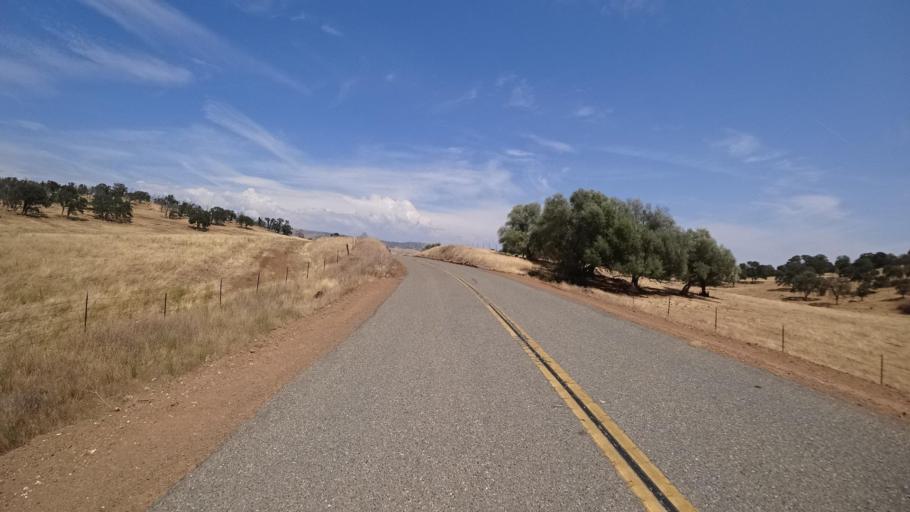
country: US
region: California
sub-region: Merced County
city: Planada
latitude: 37.5202
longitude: -120.2261
